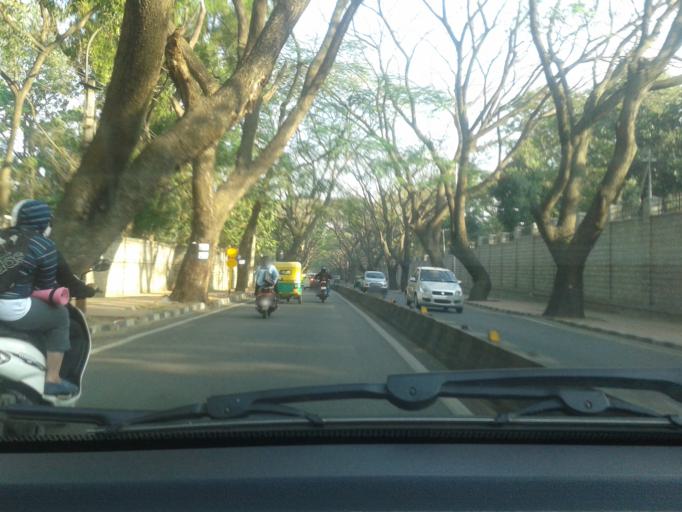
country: IN
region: Karnataka
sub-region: Bangalore Urban
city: Bangalore
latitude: 13.0179
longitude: 77.5725
